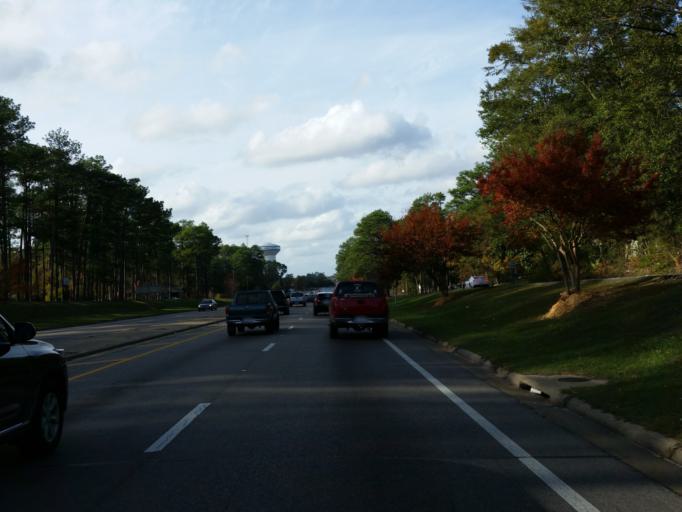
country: US
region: Mississippi
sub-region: Forrest County
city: Hattiesburg
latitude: 31.3129
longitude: -89.3222
